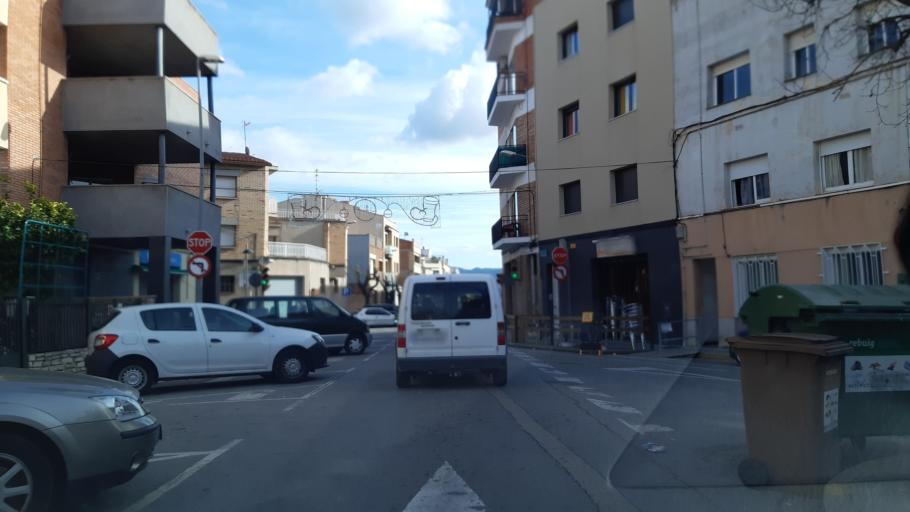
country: ES
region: Catalonia
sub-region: Provincia de Barcelona
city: Vilanova del Cami
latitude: 41.5701
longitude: 1.6401
